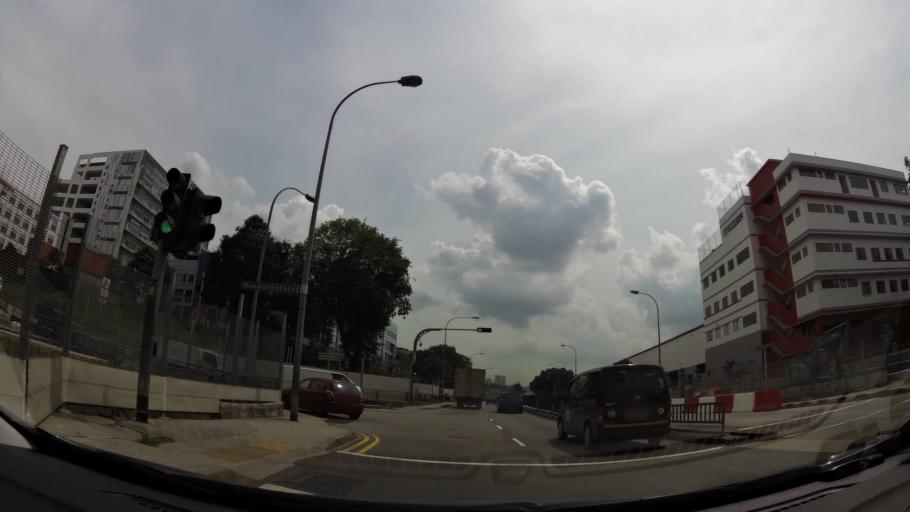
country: MY
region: Johor
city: Johor Bahru
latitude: 1.4076
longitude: 103.7562
